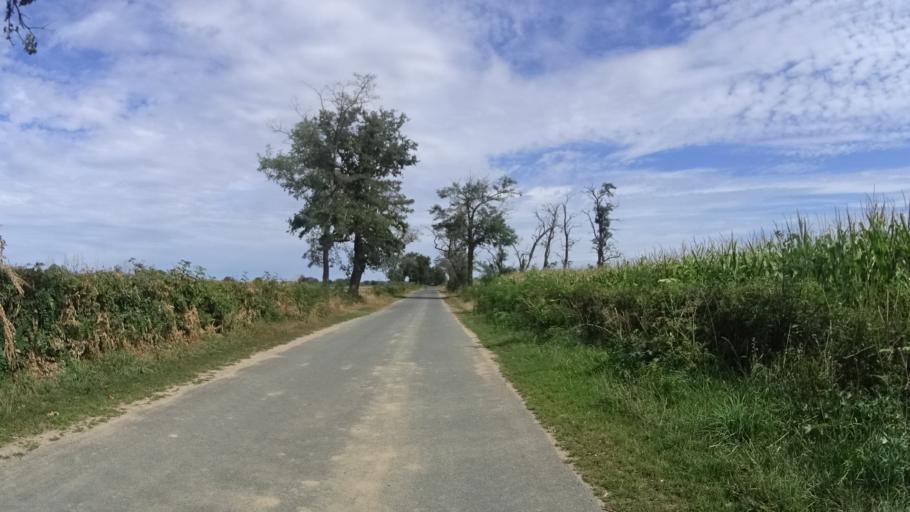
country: FR
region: Auvergne
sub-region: Departement de l'Allier
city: Beaulon
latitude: 46.6338
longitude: 3.6941
